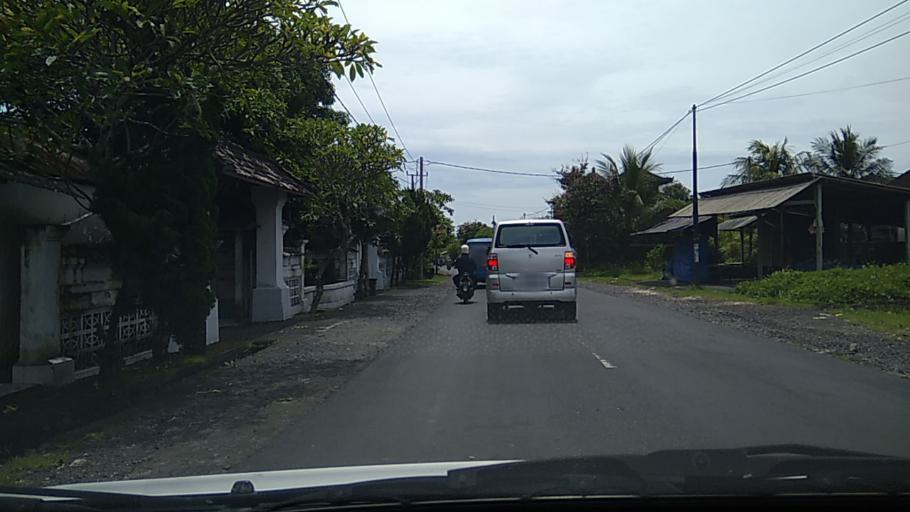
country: ID
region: Bali
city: Banjar Laing
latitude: -8.5842
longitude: 115.1257
